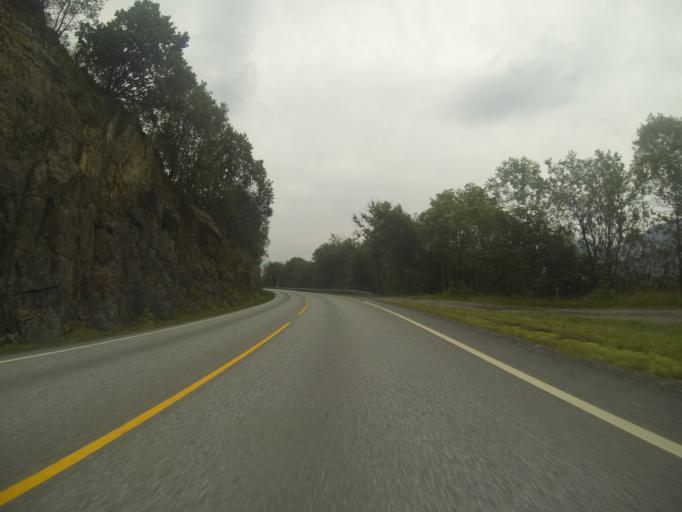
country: NO
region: Rogaland
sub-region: Suldal
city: Sand
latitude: 59.5603
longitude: 6.2677
